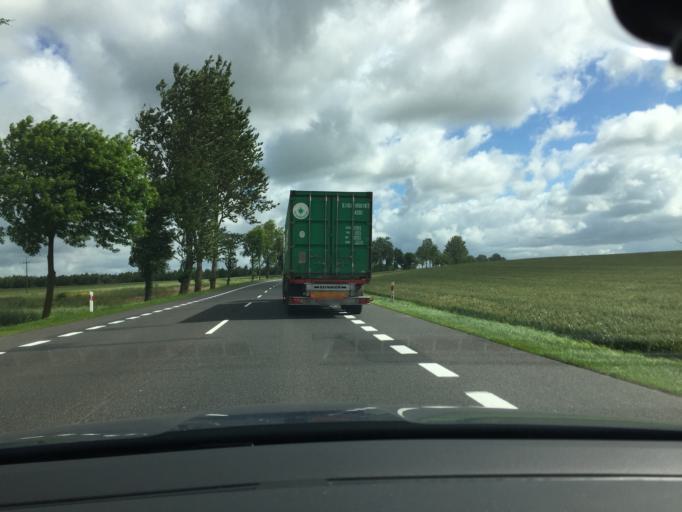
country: PL
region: West Pomeranian Voivodeship
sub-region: Powiat slawienski
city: Darlowo
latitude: 54.3135
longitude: 16.5226
